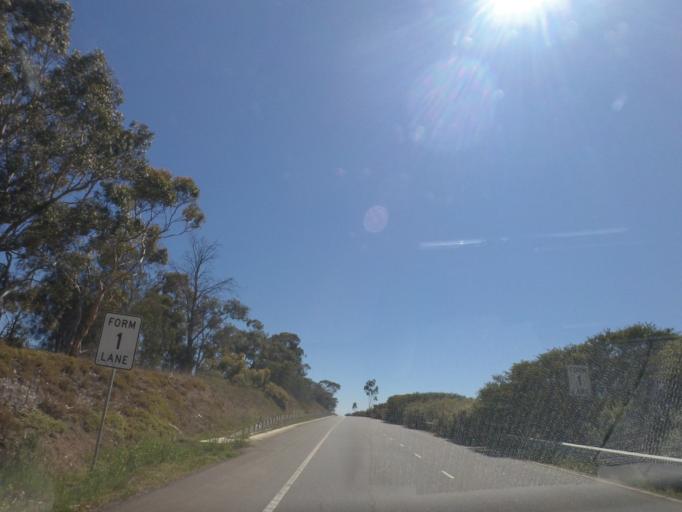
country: AU
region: Victoria
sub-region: Hume
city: Craigieburn
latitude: -37.5710
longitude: 144.9402
